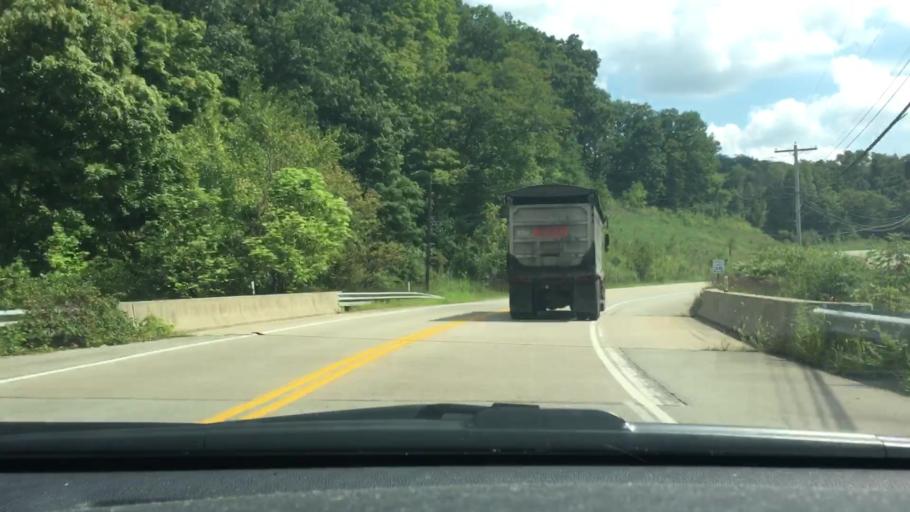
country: US
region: Pennsylvania
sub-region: Washington County
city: Gastonville
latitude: 40.2547
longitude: -79.9865
